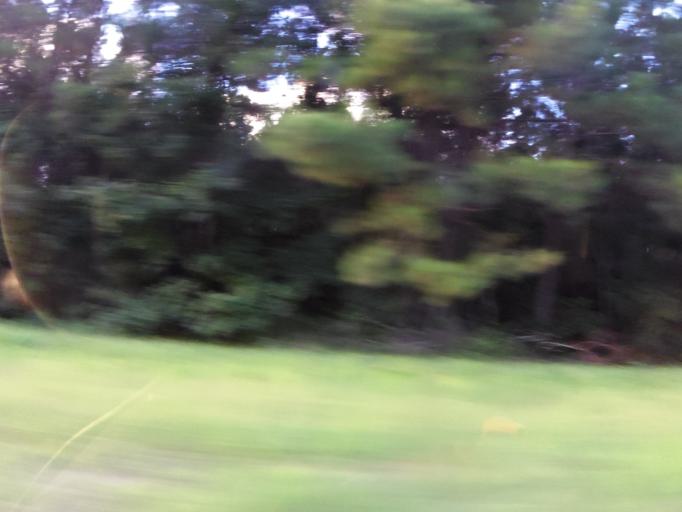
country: US
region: Georgia
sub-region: Camden County
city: Woodbine
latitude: 31.1070
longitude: -81.6616
